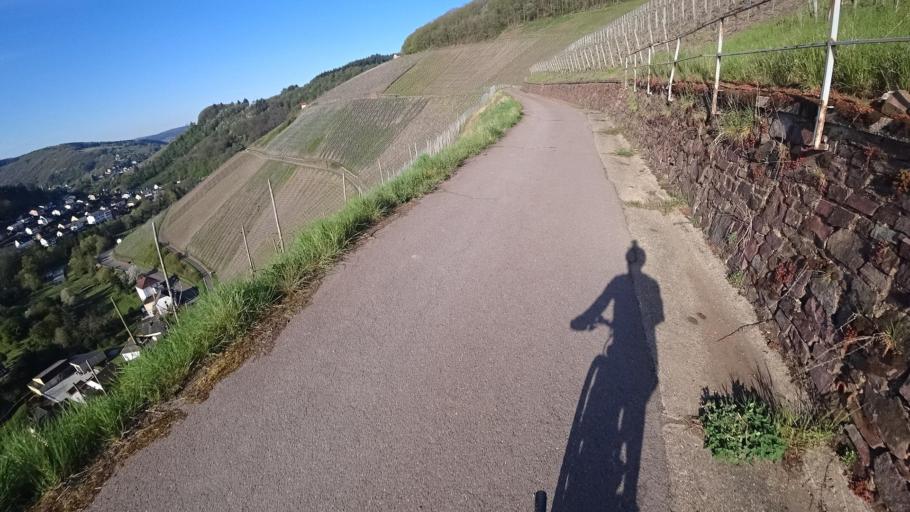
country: DE
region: Rheinland-Pfalz
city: Ayl
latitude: 49.6188
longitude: 6.5578
